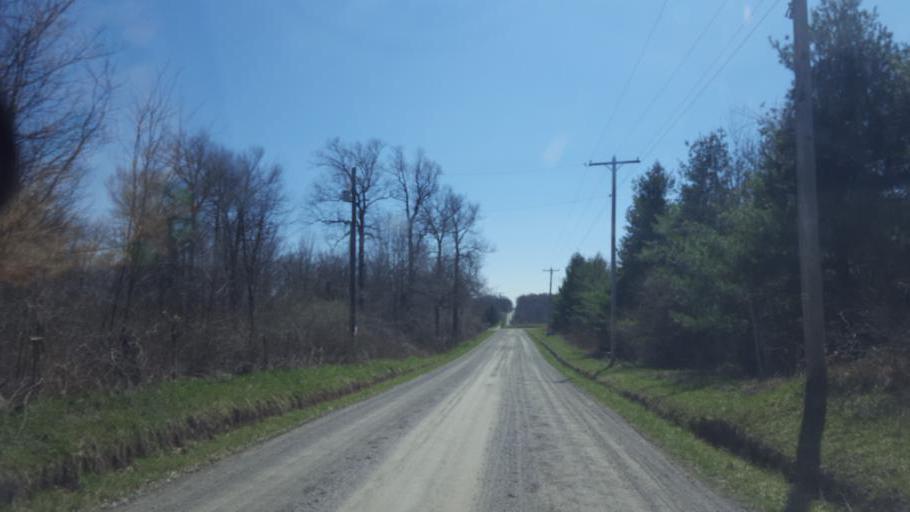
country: US
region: Ohio
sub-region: Ashland County
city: Ashland
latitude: 40.9037
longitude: -82.3586
